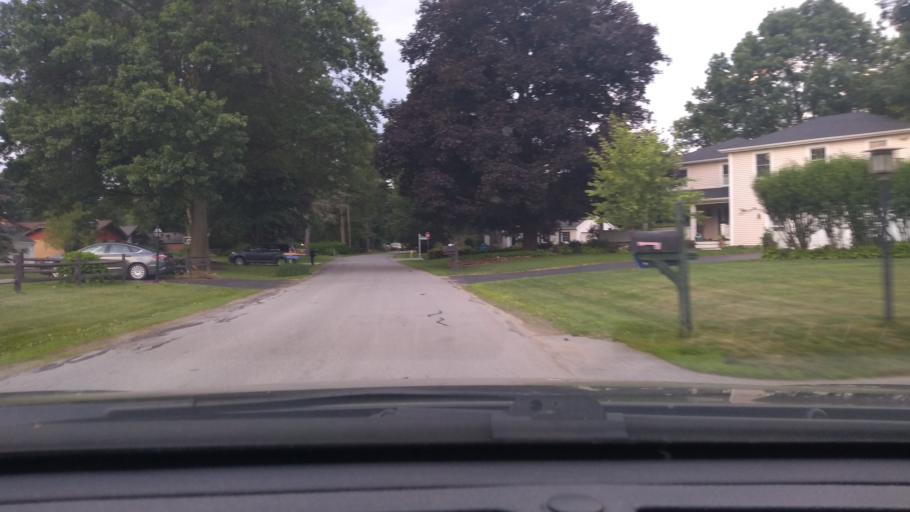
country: US
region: New York
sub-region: Erie County
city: Billington Heights
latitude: 42.7783
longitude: -78.6183
